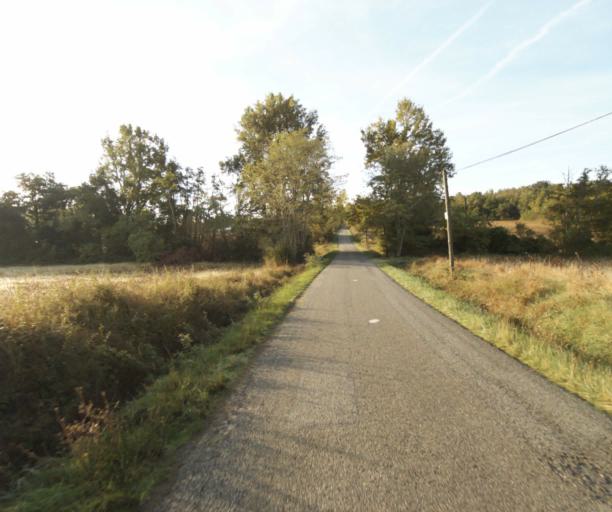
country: FR
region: Midi-Pyrenees
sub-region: Departement du Tarn-et-Garonne
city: Saint-Nauphary
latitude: 43.9442
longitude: 1.4419
